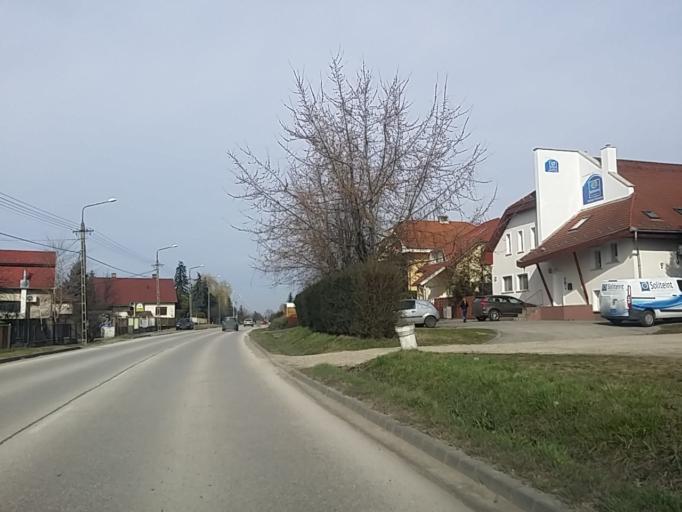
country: HU
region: Pest
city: Fot
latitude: 47.6198
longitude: 19.1906
